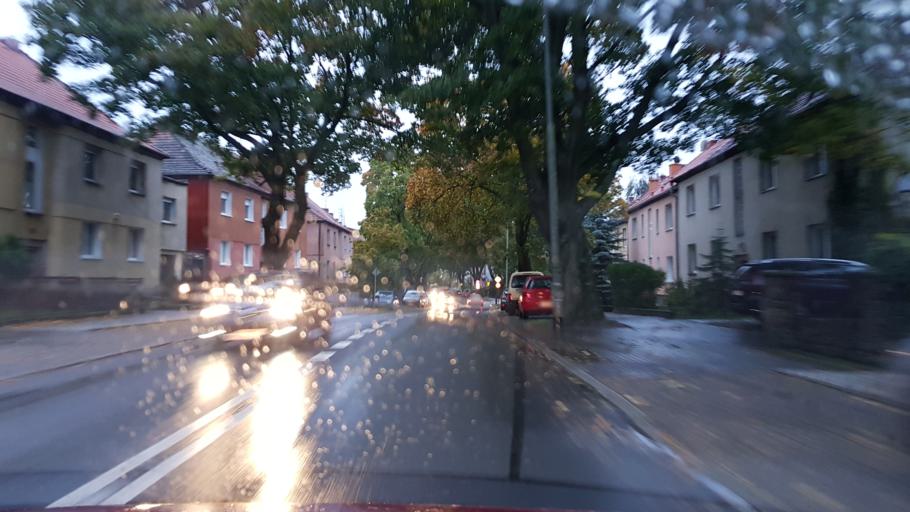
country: PL
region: West Pomeranian Voivodeship
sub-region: Szczecin
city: Szczecin
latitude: 53.4367
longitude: 14.5124
